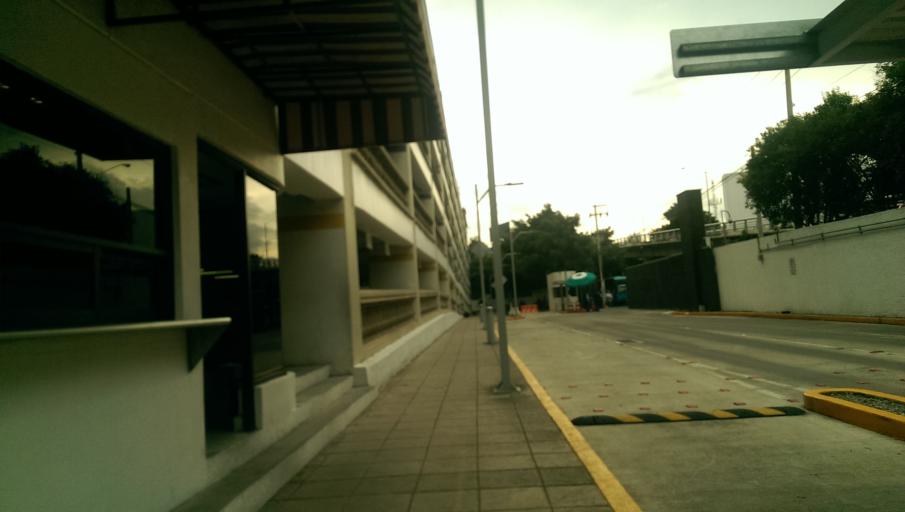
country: MX
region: Mexico City
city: Tlalpan
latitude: 19.2837
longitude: -99.1376
